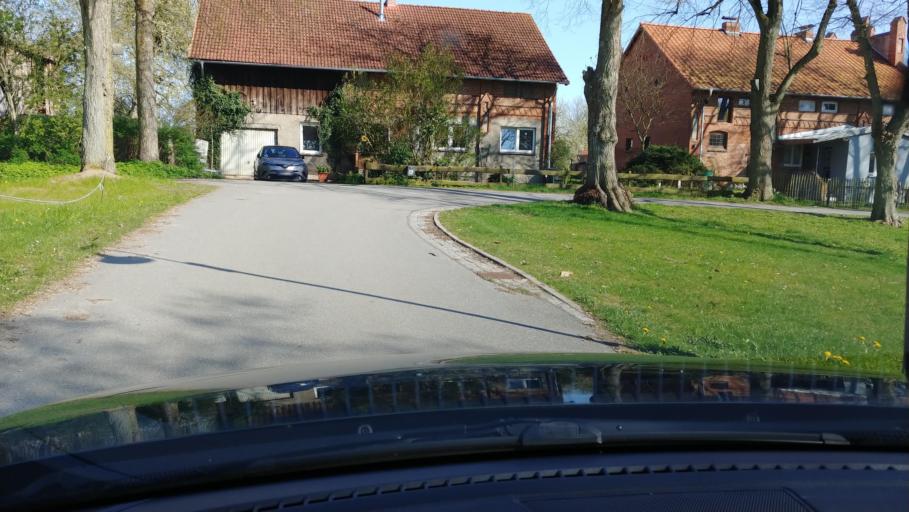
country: DE
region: Mecklenburg-Vorpommern
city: Muhlen Eichsen
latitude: 53.7974
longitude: 11.2895
